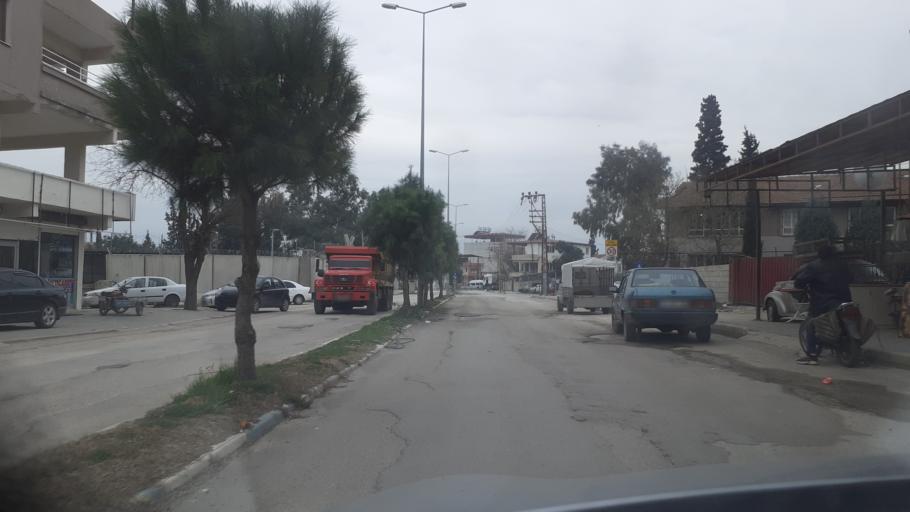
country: TR
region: Hatay
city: Kirikhan
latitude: 36.4926
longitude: 36.3580
